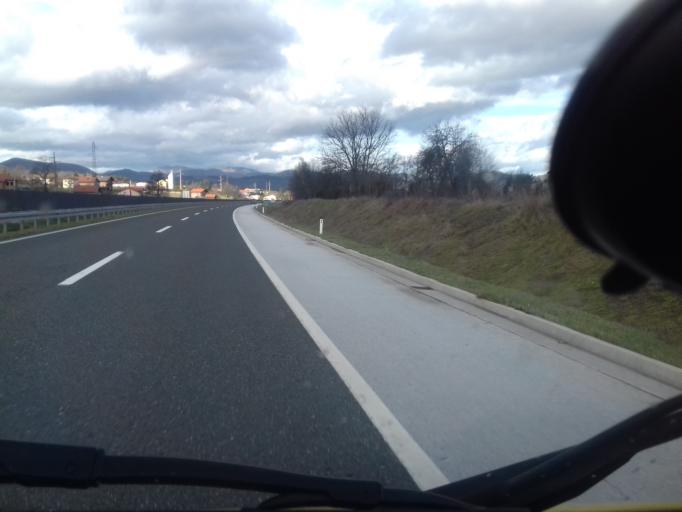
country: BA
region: Federation of Bosnia and Herzegovina
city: Gornje Mostre
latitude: 44.0091
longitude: 18.1448
